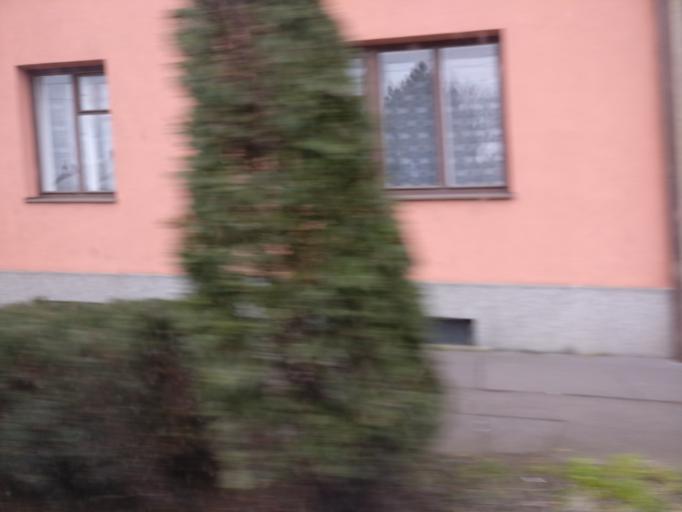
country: CZ
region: Pardubicky
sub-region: Okres Pardubice
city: Pardubice
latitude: 50.0342
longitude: 15.7899
